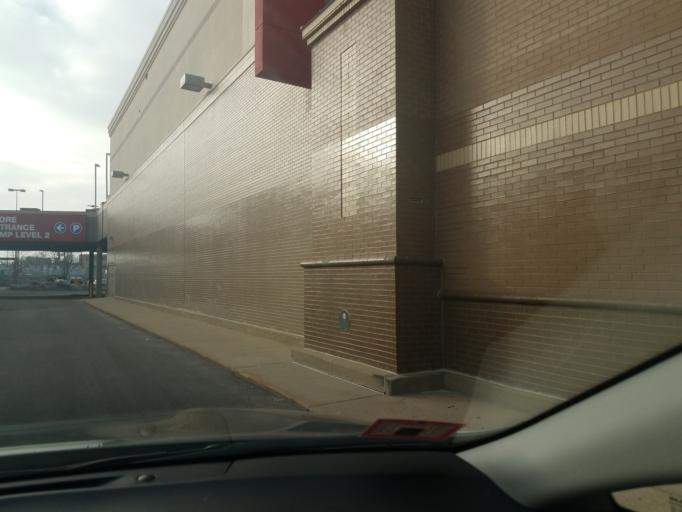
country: US
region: Illinois
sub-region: Cook County
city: Lincolnwood
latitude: 41.9455
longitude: -87.7018
